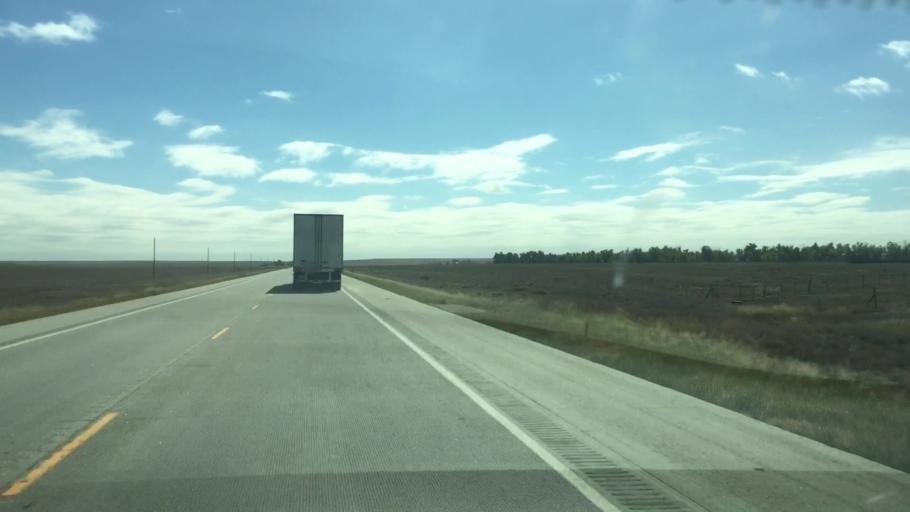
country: US
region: Colorado
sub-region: Lincoln County
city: Hugo
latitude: 39.0653
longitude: -103.3682
